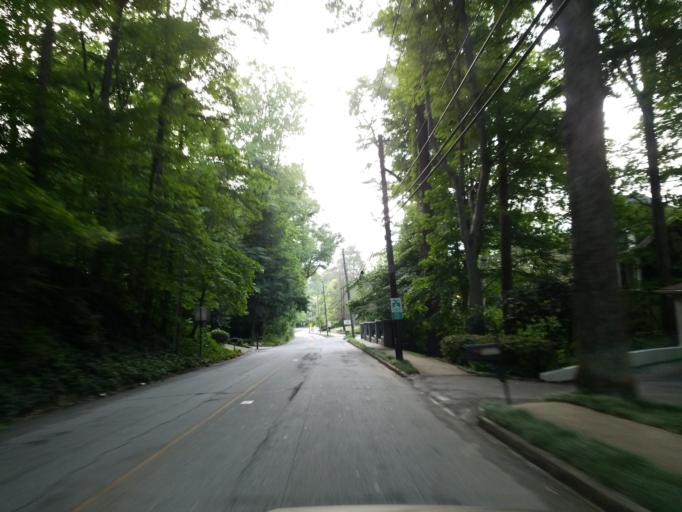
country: US
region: Georgia
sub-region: DeKalb County
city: North Atlanta
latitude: 33.8611
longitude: -84.3888
